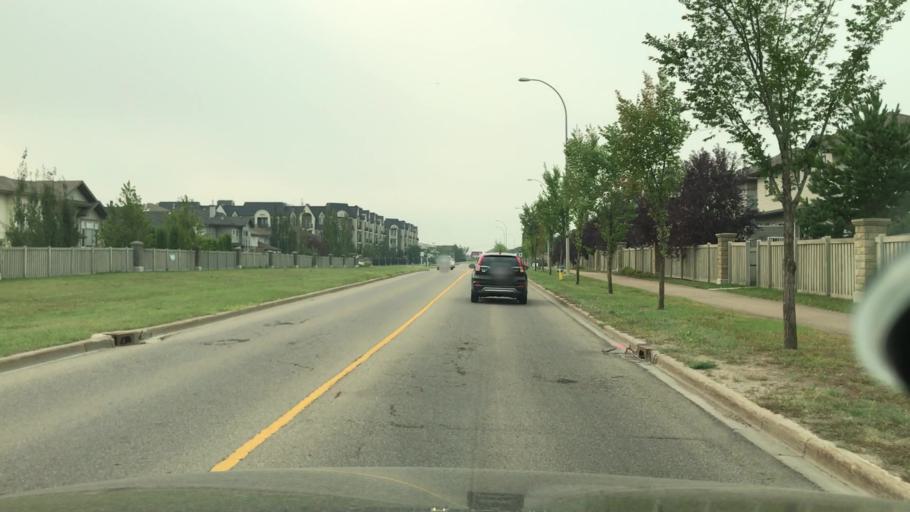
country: CA
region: Alberta
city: Edmonton
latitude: 53.4432
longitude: -113.5658
